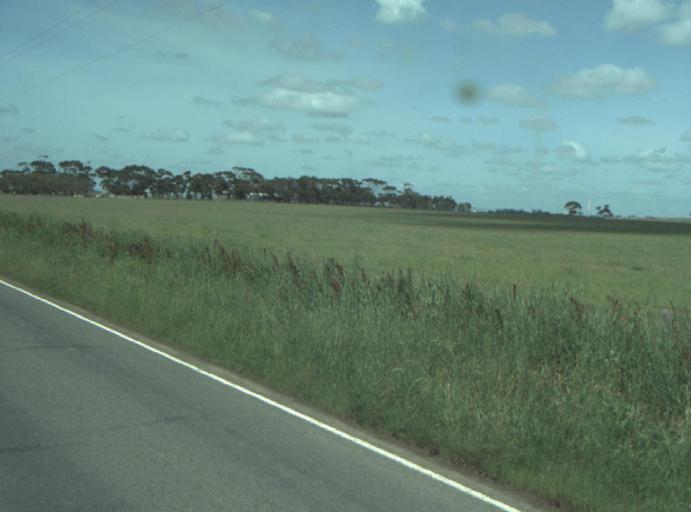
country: AU
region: Victoria
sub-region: Greater Geelong
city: Lara
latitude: -38.0500
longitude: 144.4287
